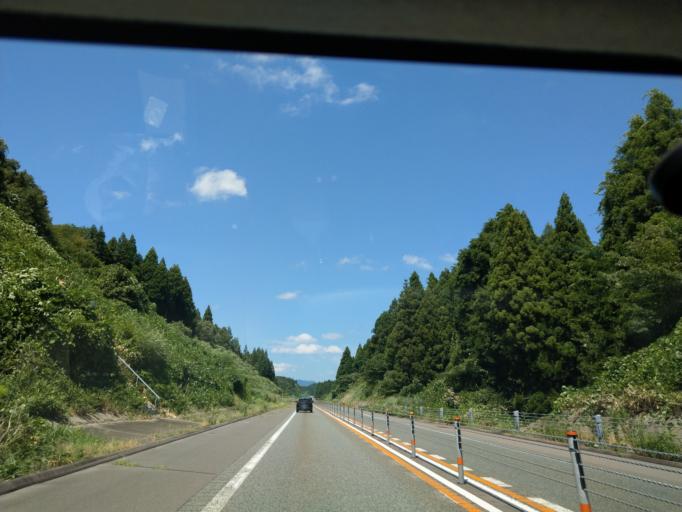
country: JP
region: Akita
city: Akita
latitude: 39.6883
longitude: 140.1857
